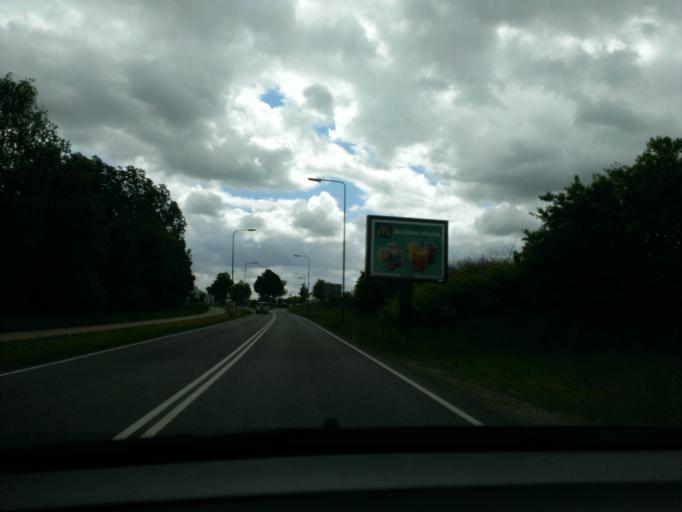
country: NL
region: Limburg
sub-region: Gemeente Heerlen
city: Nieuw-Lotbroek
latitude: 50.9068
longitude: 5.9393
